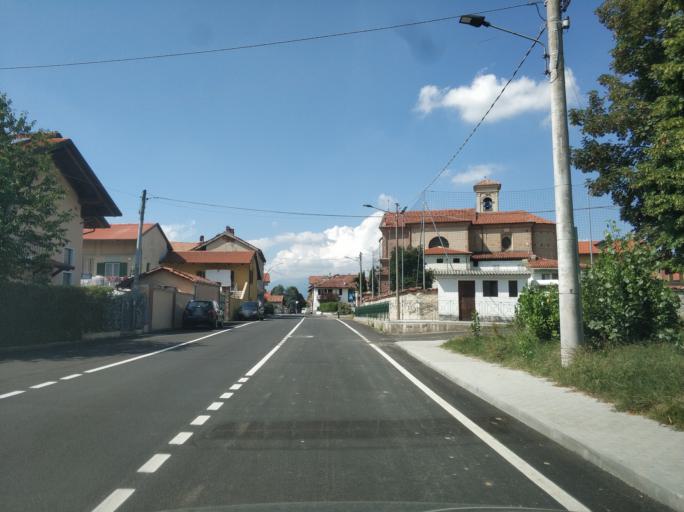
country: IT
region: Piedmont
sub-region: Provincia di Torino
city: Feletto
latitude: 45.2919
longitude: 7.7232
